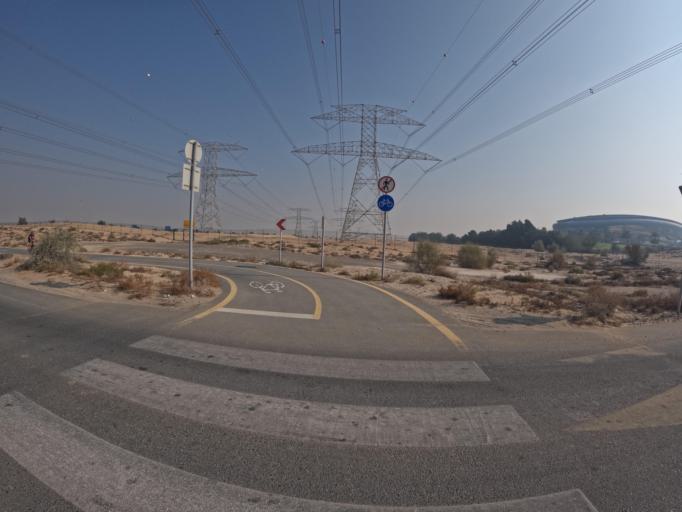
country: AE
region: Dubai
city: Dubai
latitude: 25.0520
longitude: 55.3141
